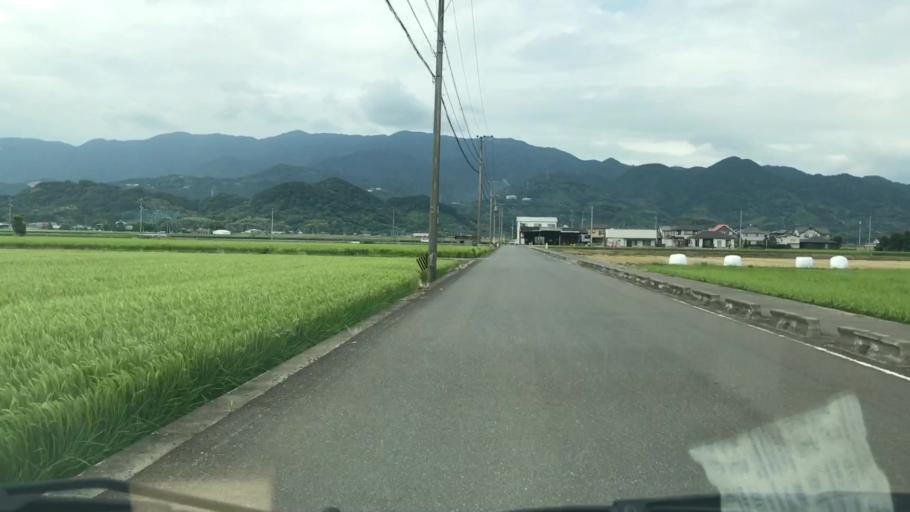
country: JP
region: Saga Prefecture
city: Saga-shi
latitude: 33.2867
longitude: 130.2251
